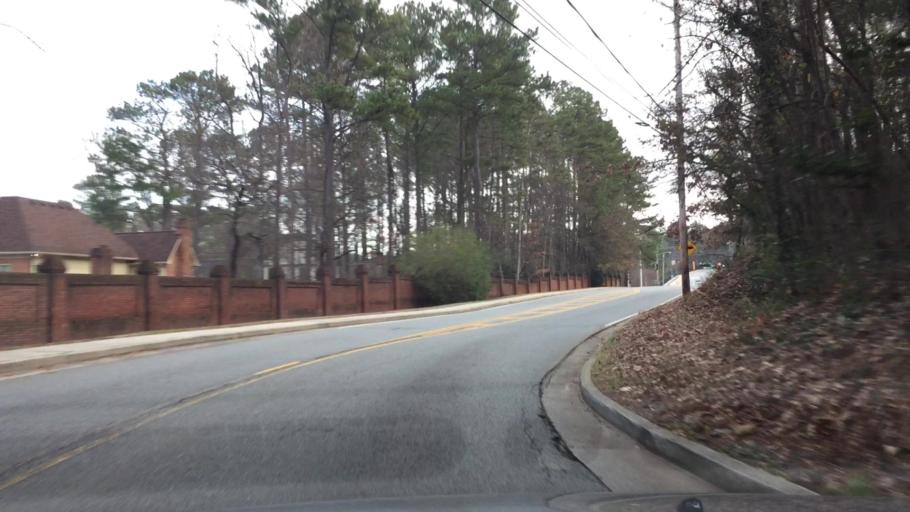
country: US
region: Georgia
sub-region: DeKalb County
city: Dunwoody
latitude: 33.9706
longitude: -84.3414
